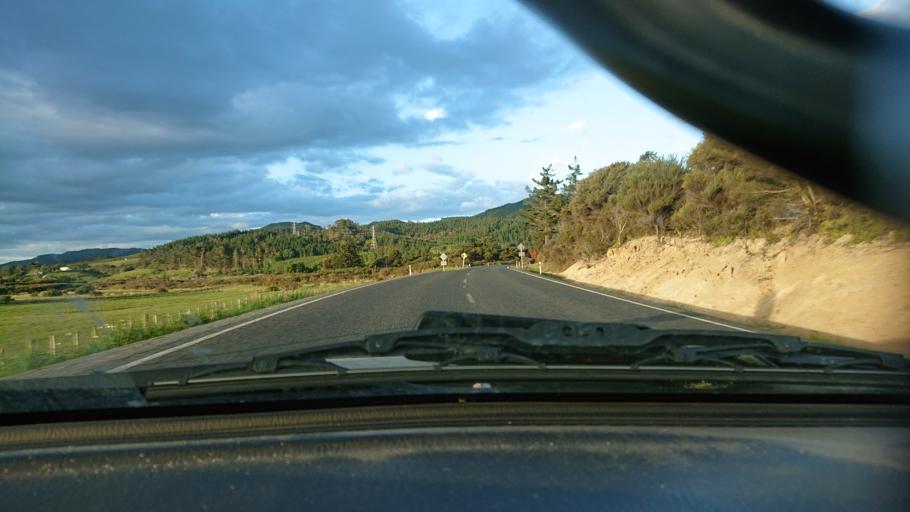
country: NZ
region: Auckland
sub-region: Auckland
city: Parakai
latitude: -36.5115
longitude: 174.4526
